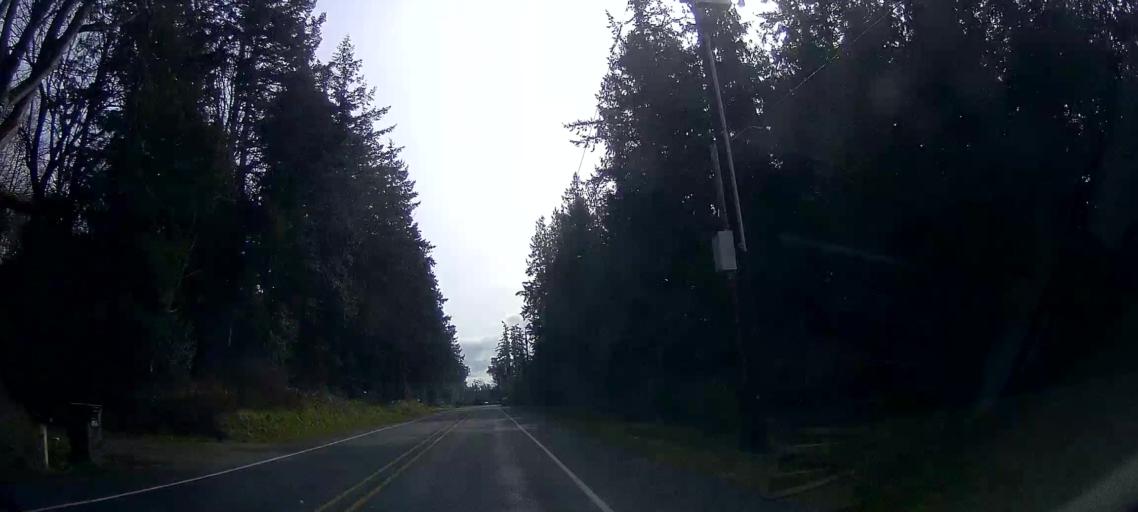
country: US
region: Washington
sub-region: Island County
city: Camano
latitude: 48.1339
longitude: -122.4646
